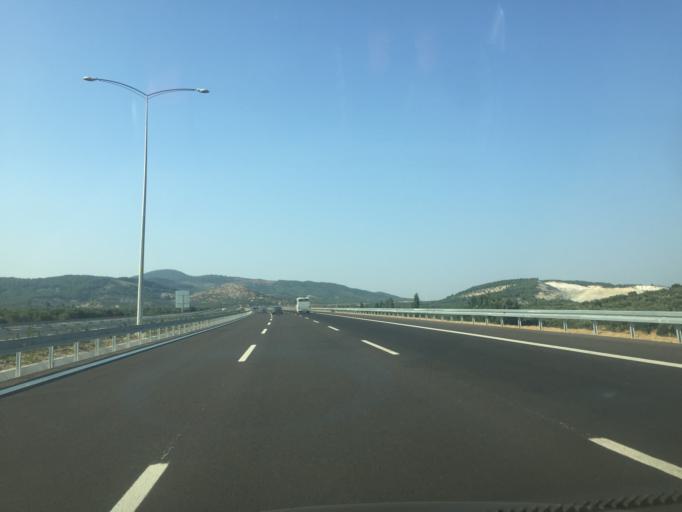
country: TR
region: Manisa
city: Zeytinliova
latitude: 38.9761
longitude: 27.7312
